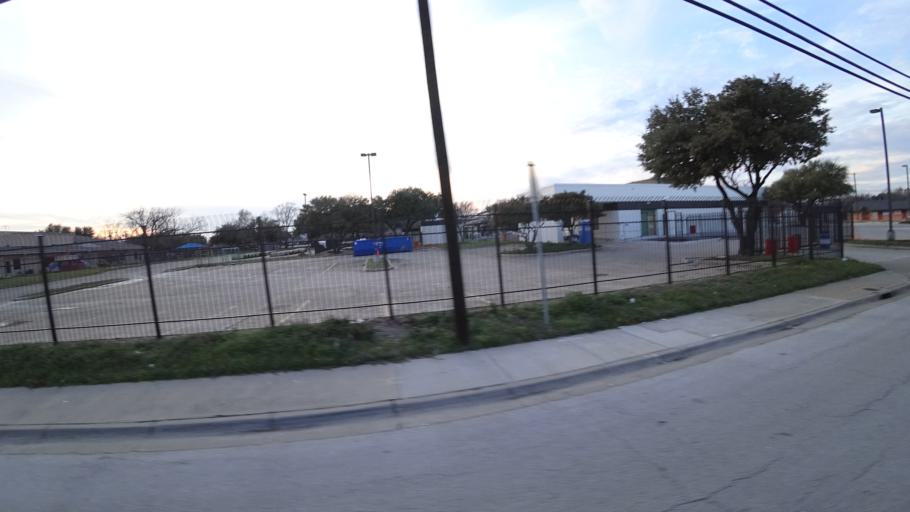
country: US
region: Texas
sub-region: Denton County
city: Lewisville
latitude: 33.0455
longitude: -97.0015
